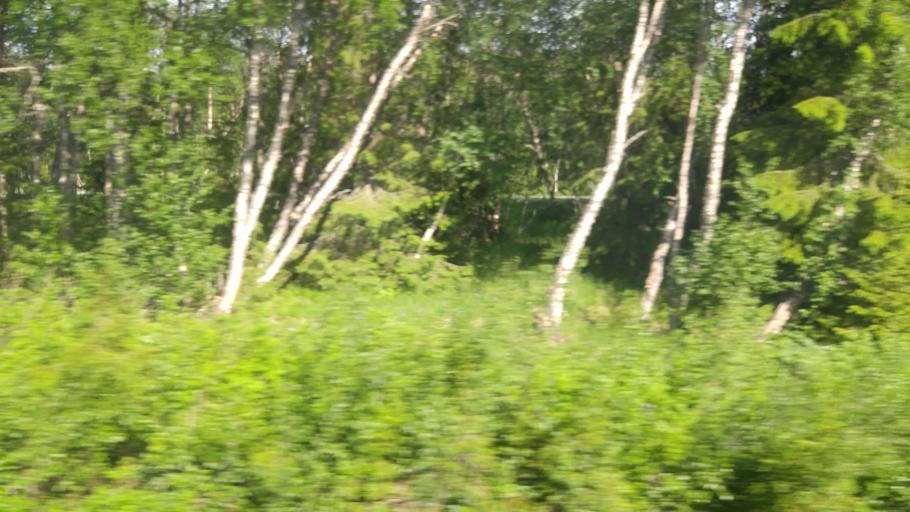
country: SE
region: Jaemtland
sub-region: Are Kommun
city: Are
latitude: 63.3600
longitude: 12.6922
